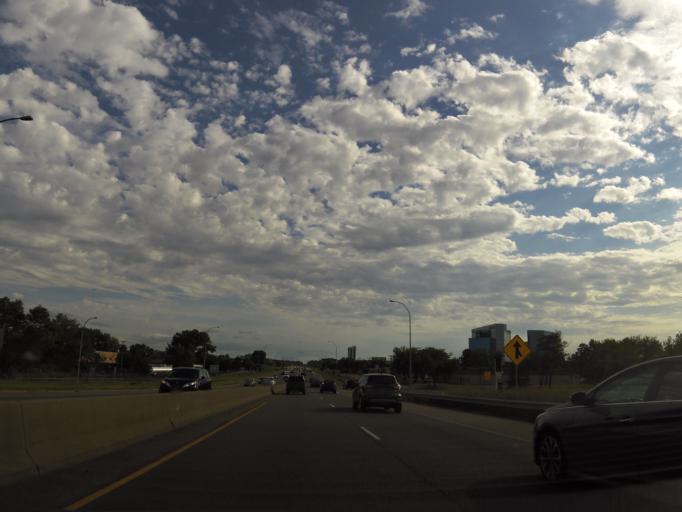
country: US
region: Minnesota
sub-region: Hennepin County
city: New Hope
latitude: 44.9907
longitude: -93.4008
